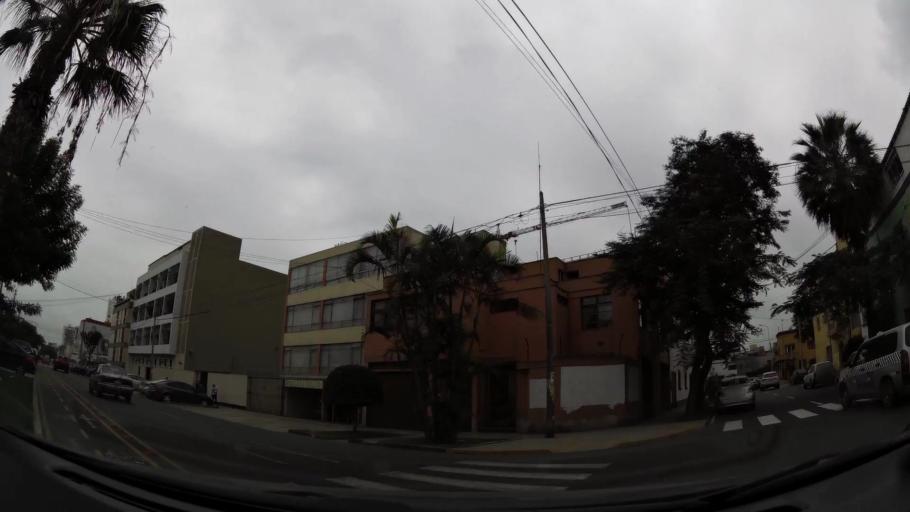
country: PE
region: Lima
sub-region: Lima
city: San Isidro
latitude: -12.0896
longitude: -77.0375
